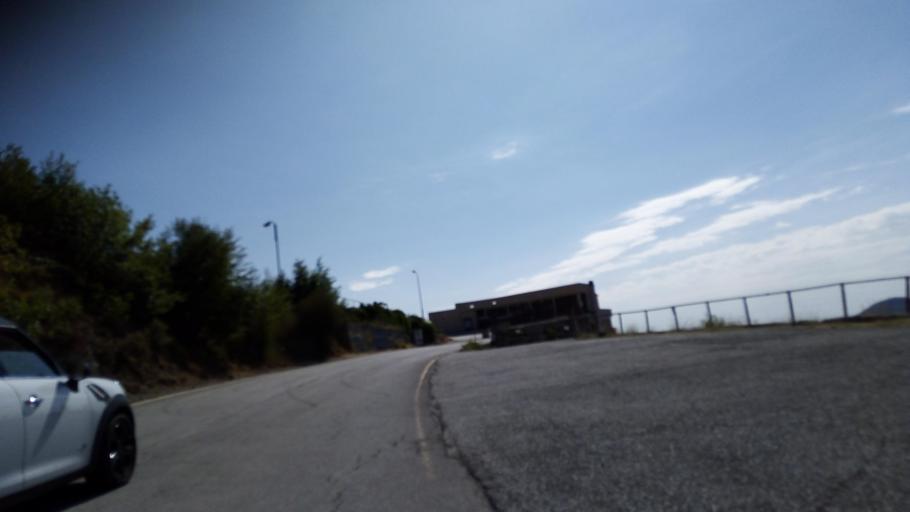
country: IT
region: Liguria
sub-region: Provincia di Savona
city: Balestrino
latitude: 44.1452
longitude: 8.1735
